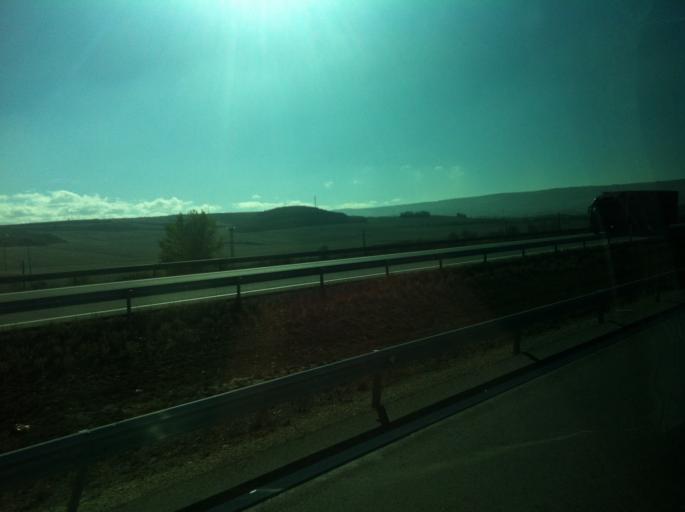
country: ES
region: Castille and Leon
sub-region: Provincia de Burgos
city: Quintanapalla
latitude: 42.4182
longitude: -3.5216
